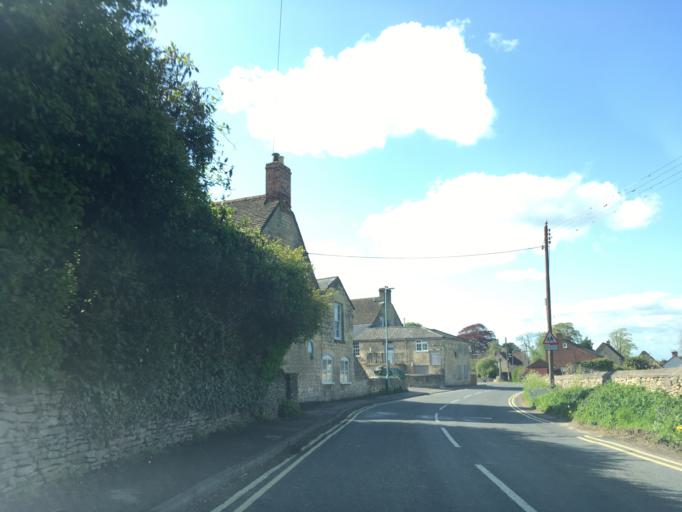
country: GB
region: England
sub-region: Gloucestershire
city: Stonehouse
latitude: 51.7294
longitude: -2.2732
